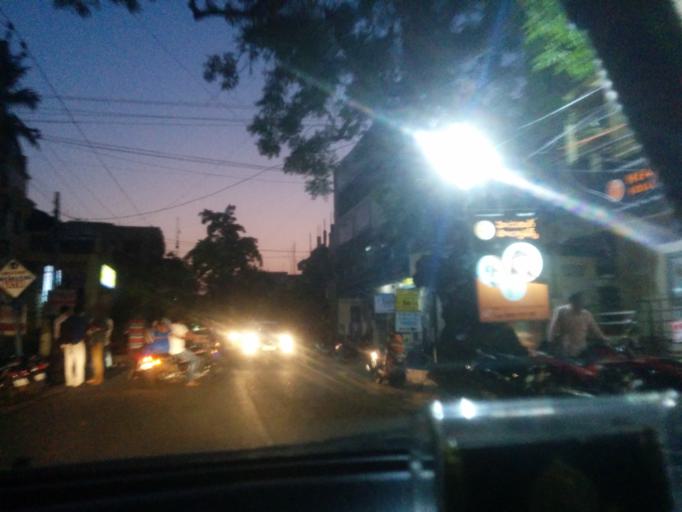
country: IN
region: Andhra Pradesh
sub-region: East Godavari
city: Rajahmundry
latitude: 17.0081
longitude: 81.7819
